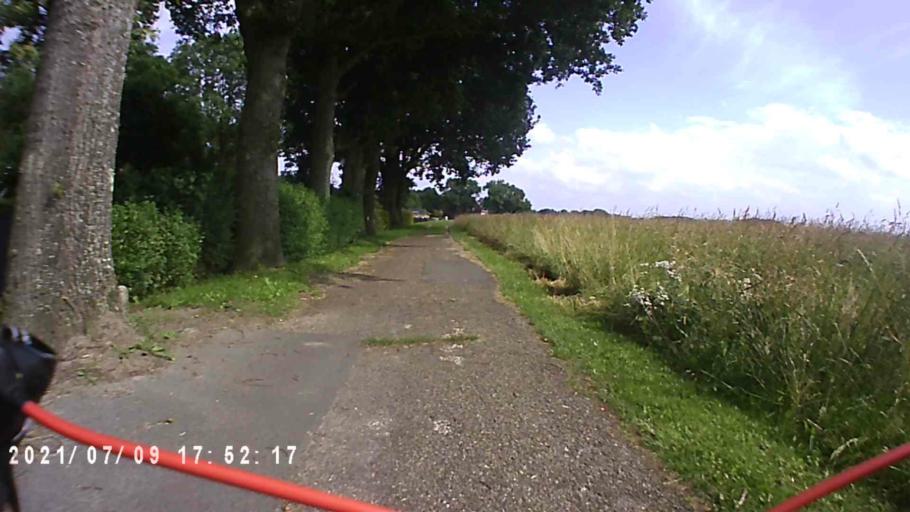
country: NL
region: Groningen
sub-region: Gemeente Vlagtwedde
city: Vlagtwedde
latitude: 53.0670
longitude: 7.0779
